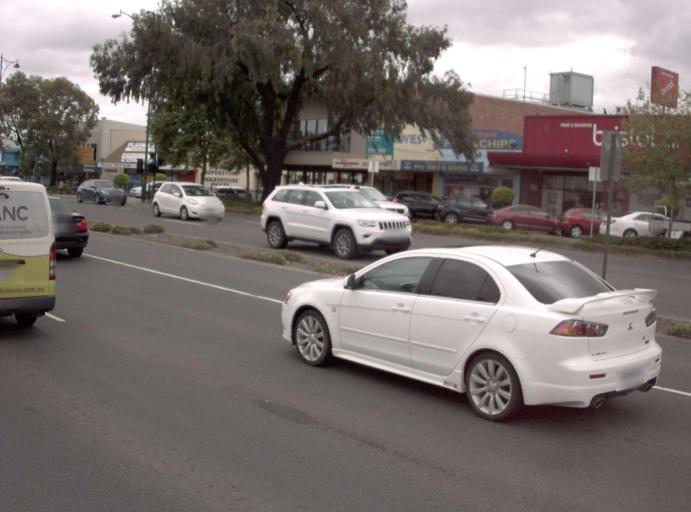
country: AU
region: Victoria
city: Mitcham
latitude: -37.8163
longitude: 145.1945
